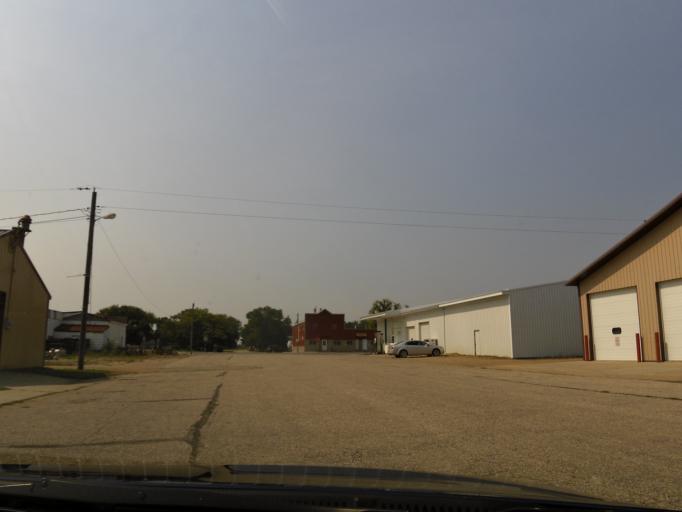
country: US
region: South Dakota
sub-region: Roberts County
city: Sisseton
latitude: 45.8568
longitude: -97.1026
